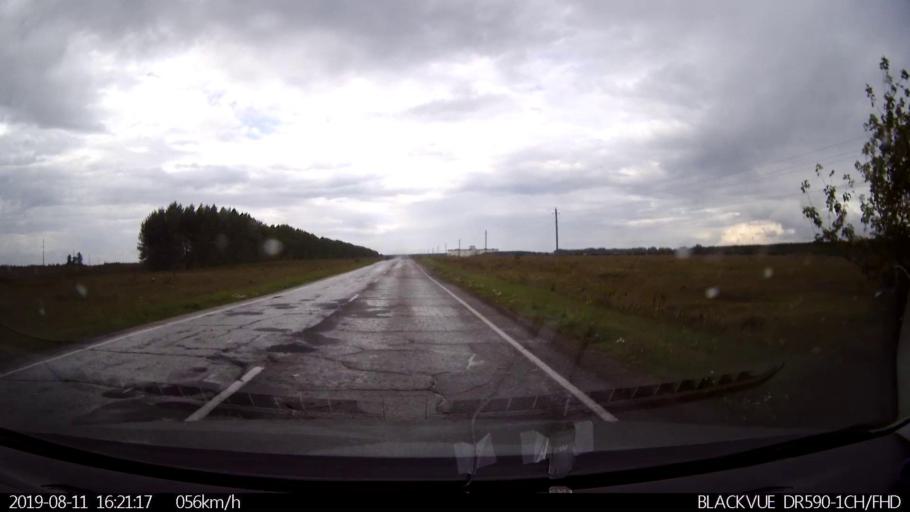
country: RU
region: Ulyanovsk
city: Mayna
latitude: 54.0786
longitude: 47.5987
